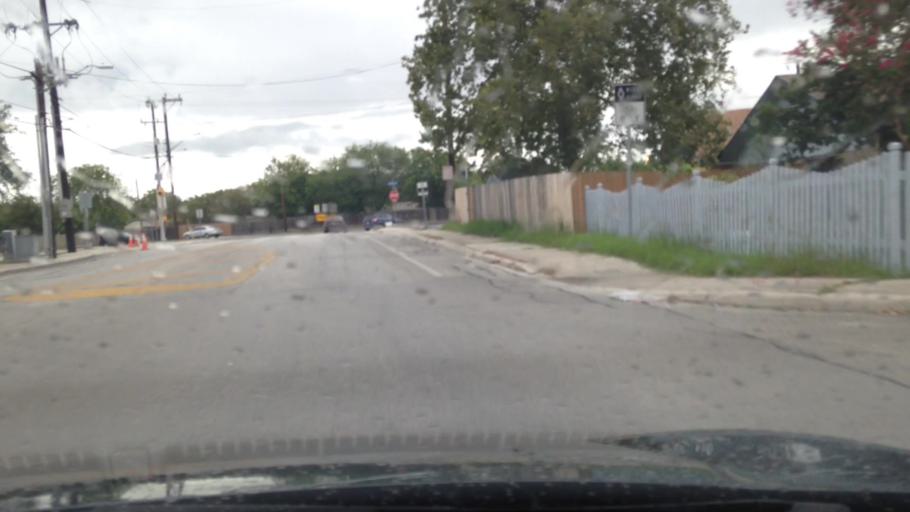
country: US
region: Texas
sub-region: Bexar County
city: Windcrest
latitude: 29.5670
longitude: -98.3949
